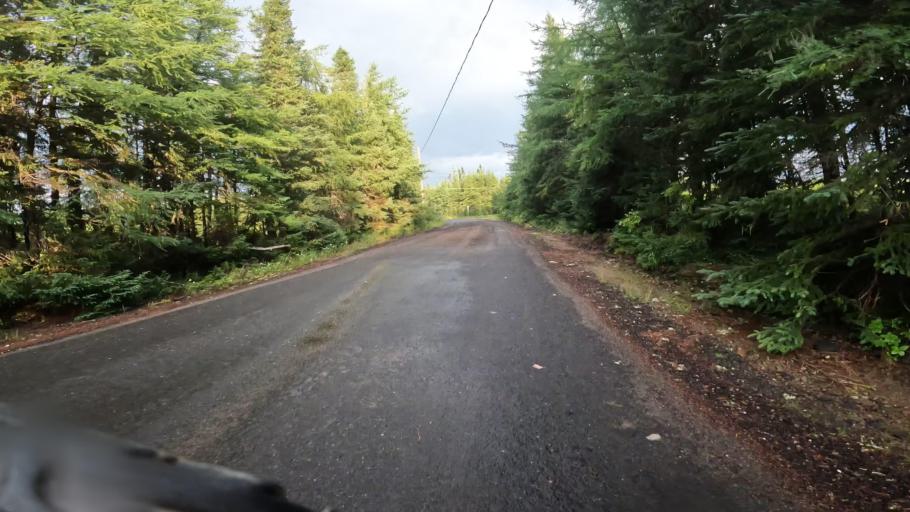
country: CA
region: Quebec
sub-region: Capitale-Nationale
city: Beaupre
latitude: 47.6385
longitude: -71.2368
